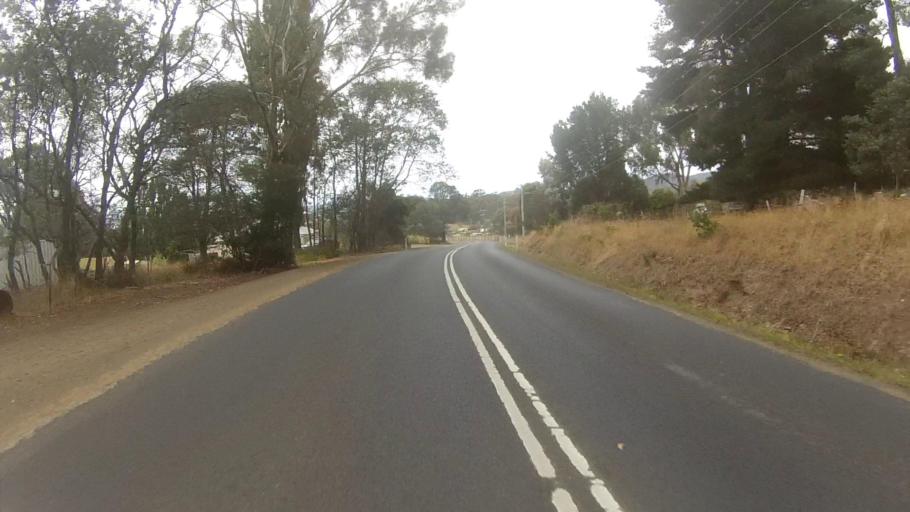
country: AU
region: Tasmania
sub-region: Kingborough
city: Margate
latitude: -43.0187
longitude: 147.2534
